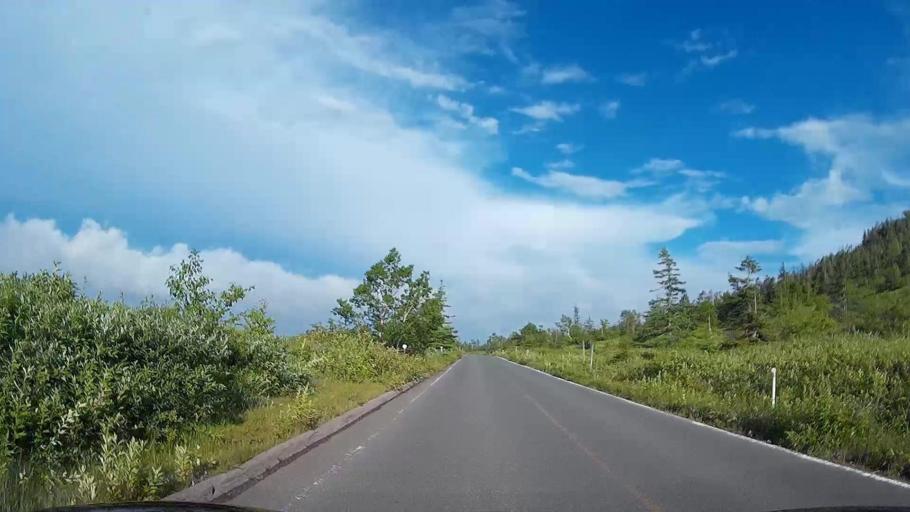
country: JP
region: Nagano
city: Nakano
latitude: 36.6375
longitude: 138.5344
